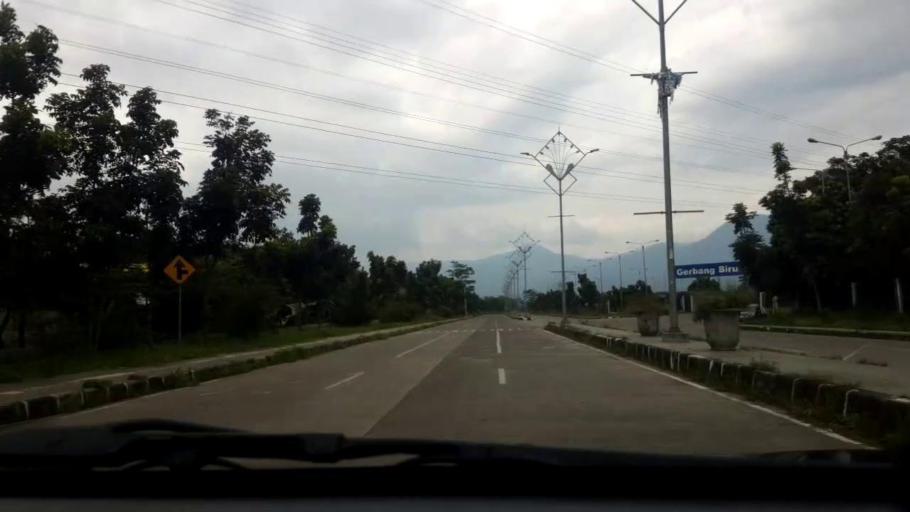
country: ID
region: West Java
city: Cileunyi
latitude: -6.9573
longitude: 107.7106
